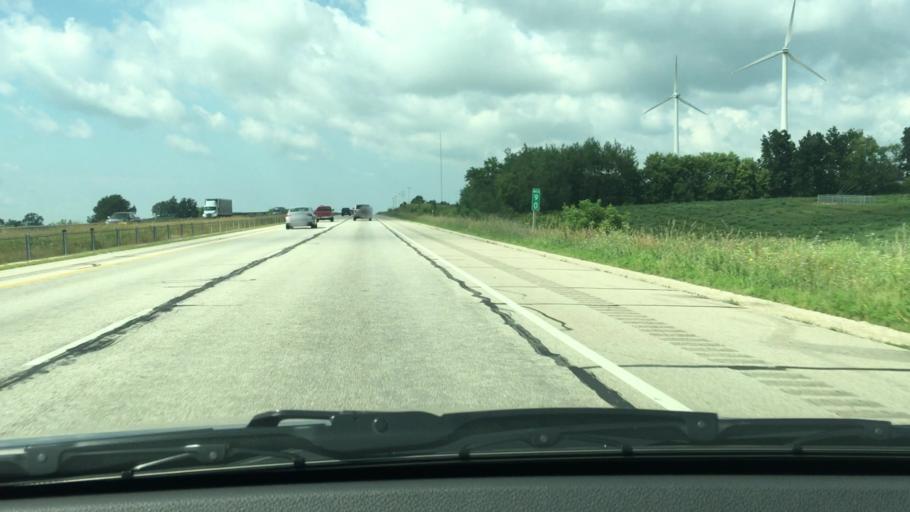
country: US
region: Wisconsin
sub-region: Dodge County
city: Lomira
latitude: 43.6535
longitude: -88.4414
